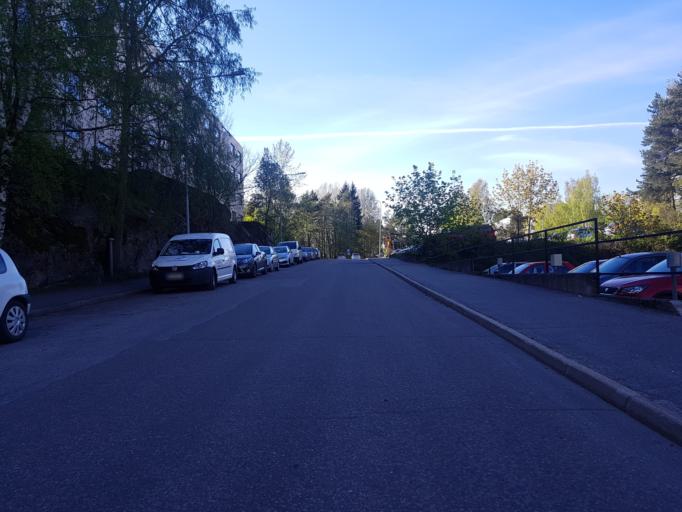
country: FI
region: Uusimaa
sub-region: Helsinki
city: Vantaa
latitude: 60.2327
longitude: 24.9981
